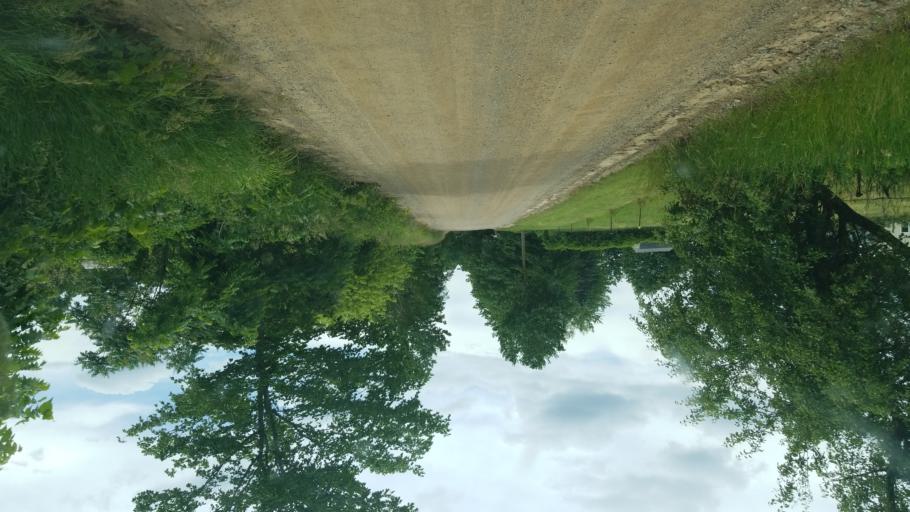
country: US
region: Michigan
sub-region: Barry County
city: Nashville
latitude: 42.6077
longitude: -84.9757
